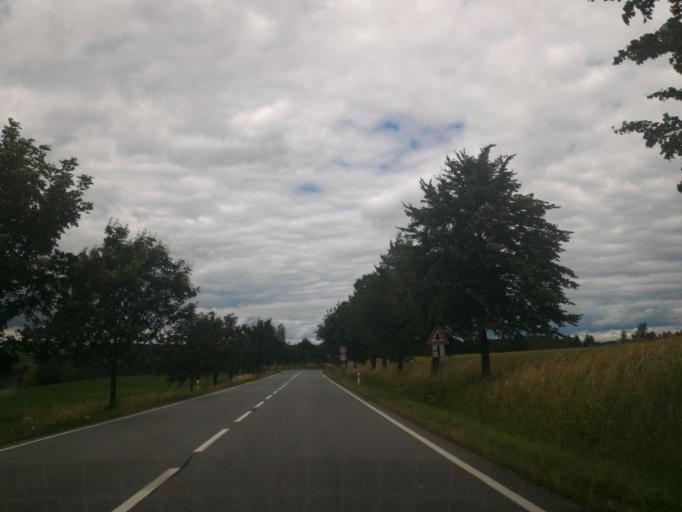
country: CZ
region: Vysocina
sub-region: Okres Pelhrimov
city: Pelhrimov
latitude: 49.4563
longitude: 15.1858
